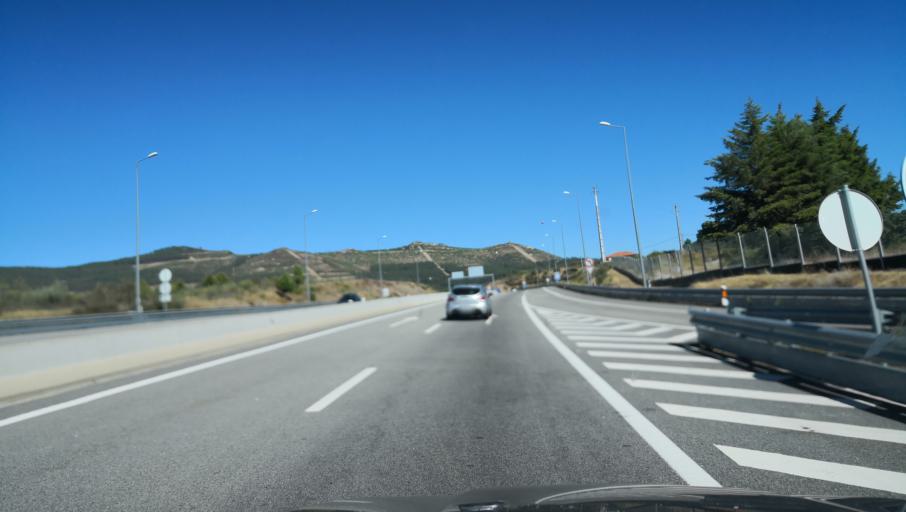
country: PT
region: Vila Real
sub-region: Murca
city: Murca
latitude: 41.4190
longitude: -7.4090
